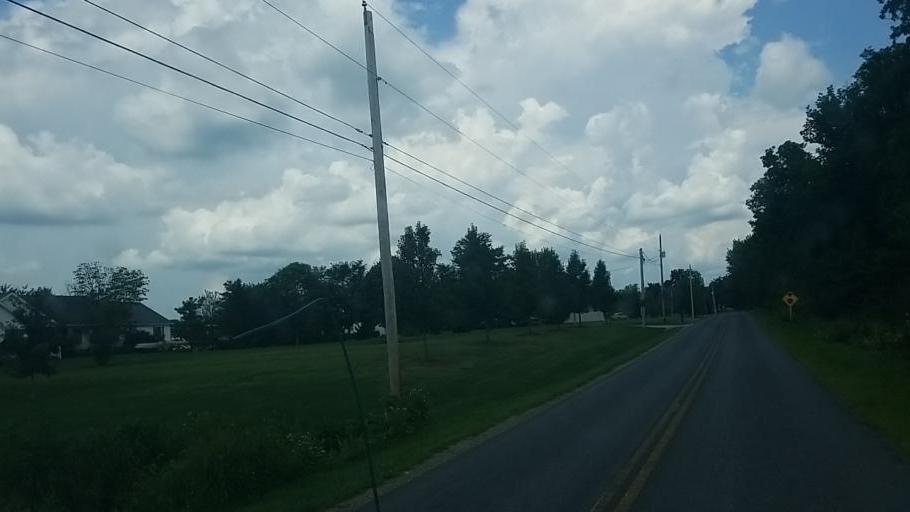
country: US
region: Ohio
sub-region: Medina County
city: Lodi
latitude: 41.0830
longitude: -82.0759
